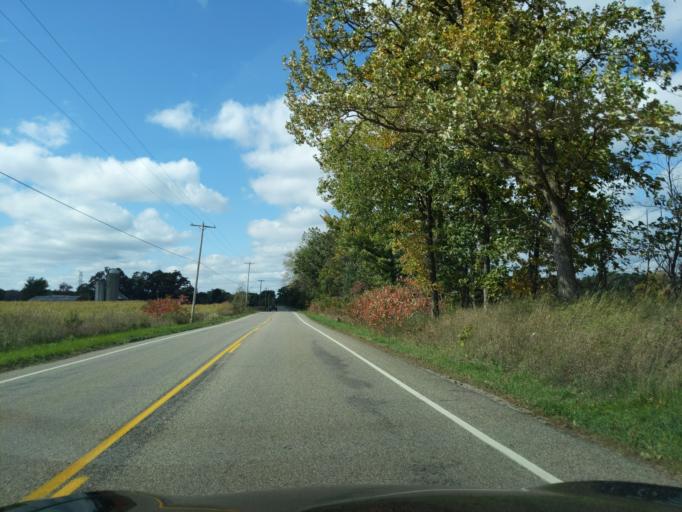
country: US
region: Michigan
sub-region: Eaton County
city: Potterville
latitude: 42.5676
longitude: -84.7645
